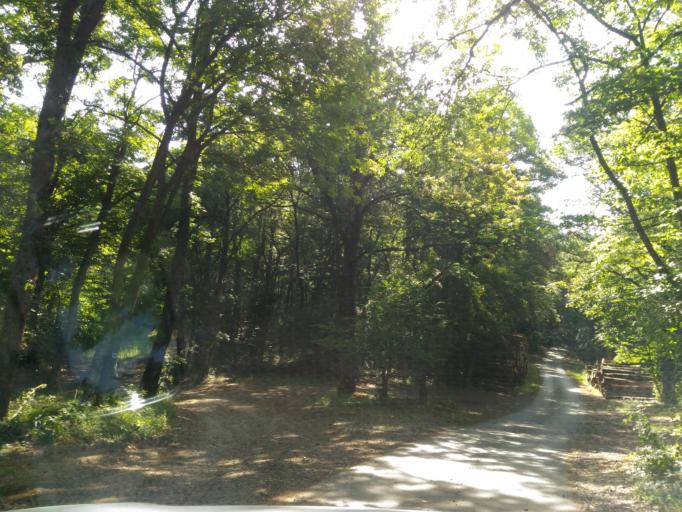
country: HU
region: Baranya
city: Hosszuheteny
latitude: 46.2149
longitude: 18.3585
